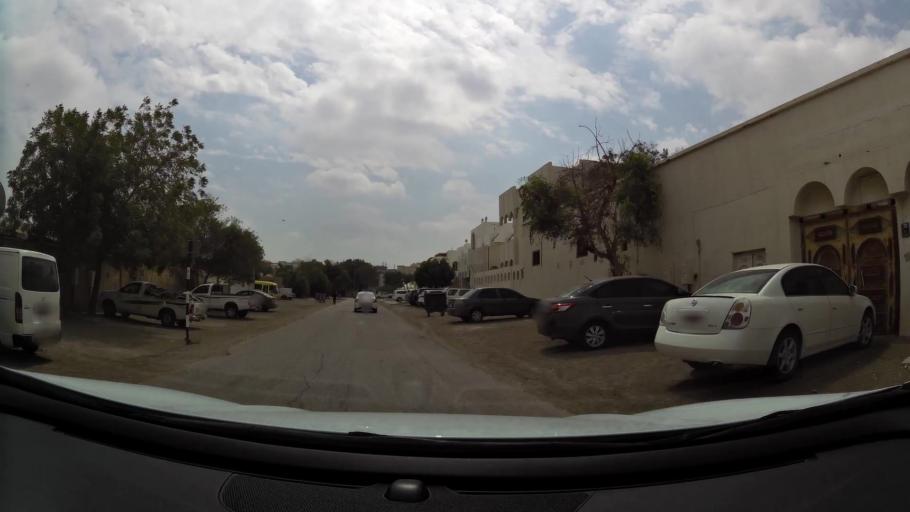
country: AE
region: Abu Dhabi
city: Al Ain
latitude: 24.2172
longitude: 55.7779
